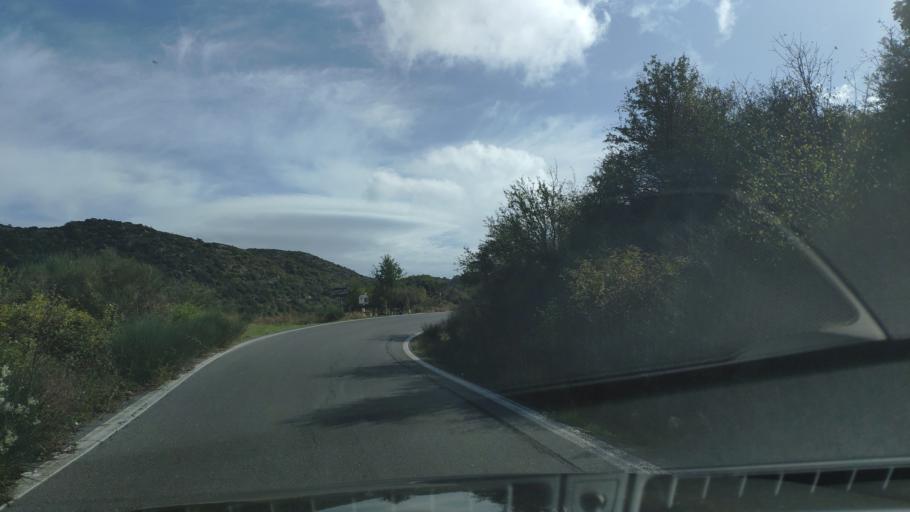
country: GR
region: Peloponnese
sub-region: Nomos Arkadias
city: Dimitsana
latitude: 37.5852
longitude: 22.0194
